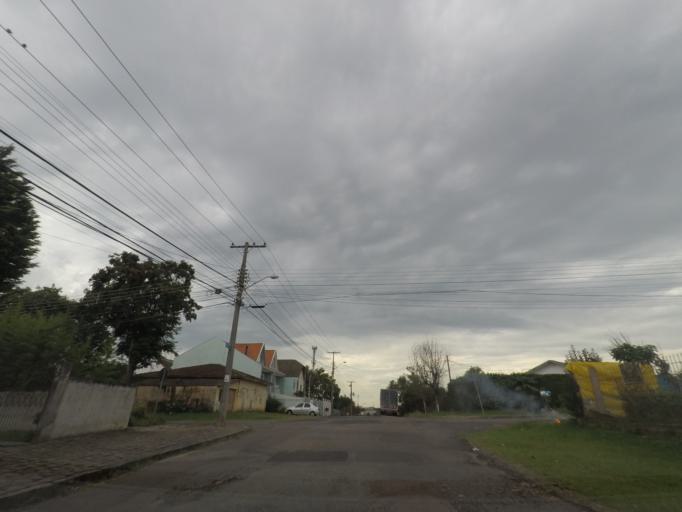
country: BR
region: Parana
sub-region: Curitiba
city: Curitiba
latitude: -25.4700
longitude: -49.3053
